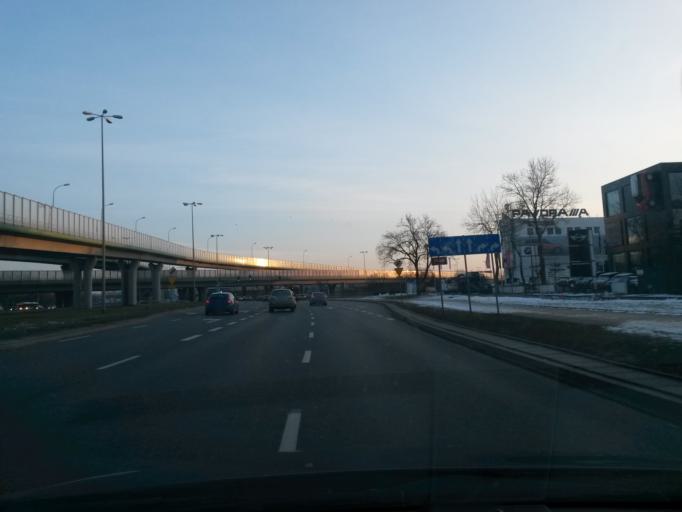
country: PL
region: Masovian Voivodeship
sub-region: Warszawa
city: Mokotow
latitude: 52.1990
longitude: 21.0506
